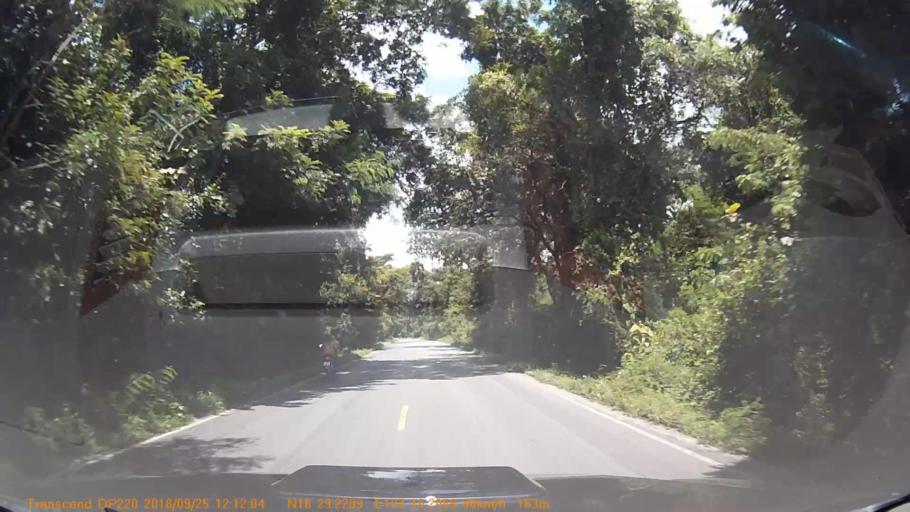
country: TH
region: Kalasin
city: Huai Mek
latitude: 16.4874
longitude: 103.2702
